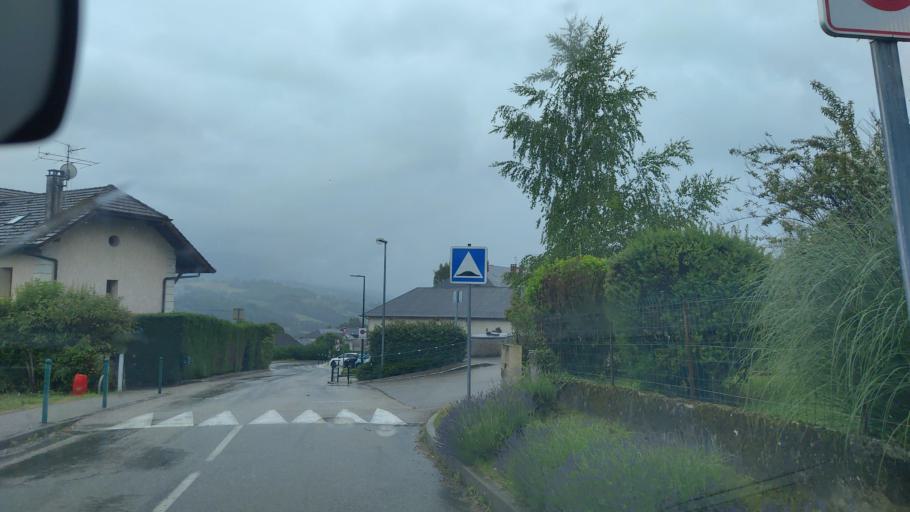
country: FR
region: Rhone-Alpes
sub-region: Departement de la Savoie
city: La Biolle
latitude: 45.7592
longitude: 5.9284
